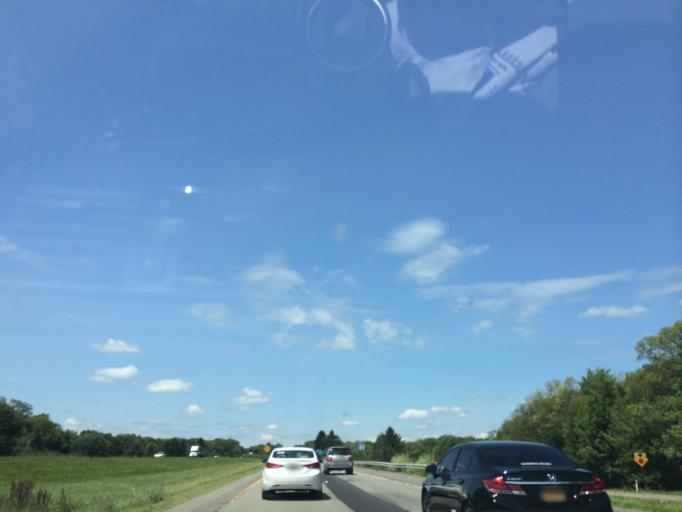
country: US
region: Pennsylvania
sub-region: Wayne County
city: Hawley
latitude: 41.3604
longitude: -75.1986
